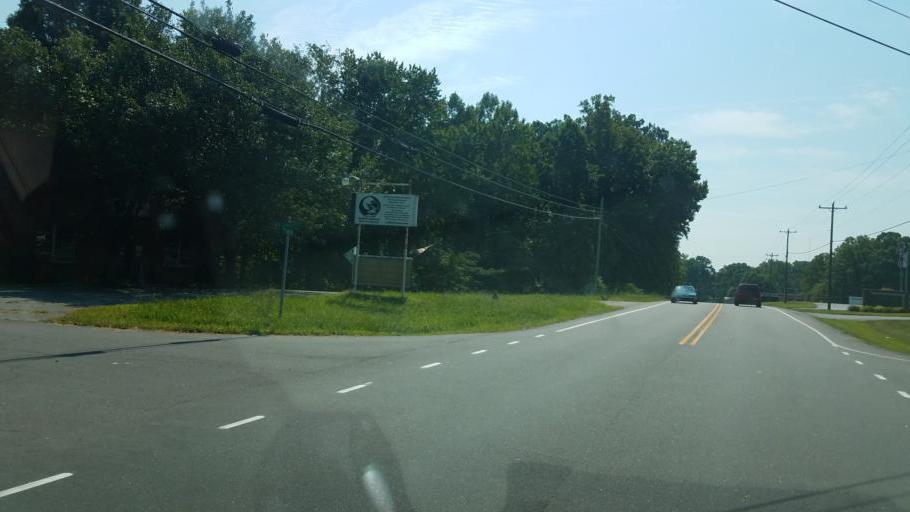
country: US
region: North Carolina
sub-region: Burke County
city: Morganton
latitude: 35.7608
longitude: -81.7352
